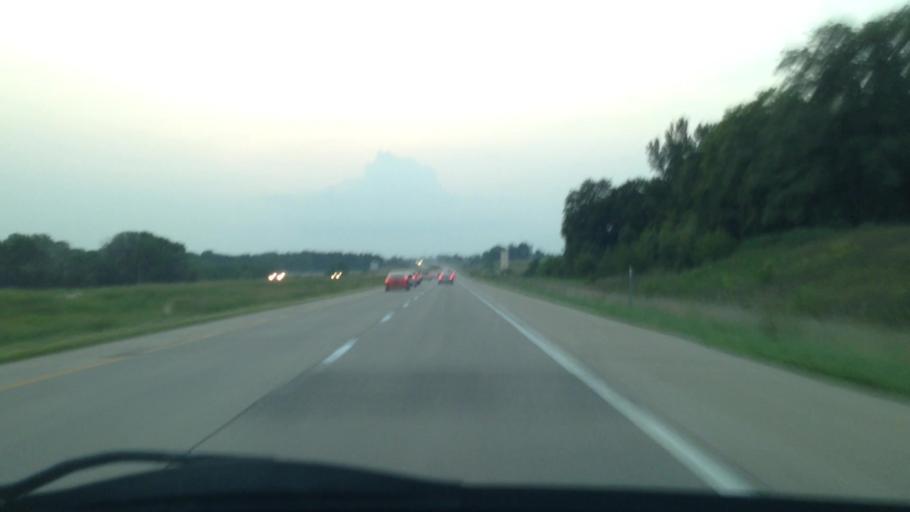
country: US
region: Iowa
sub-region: Buchanan County
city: Jesup
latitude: 42.3604
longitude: -92.0803
